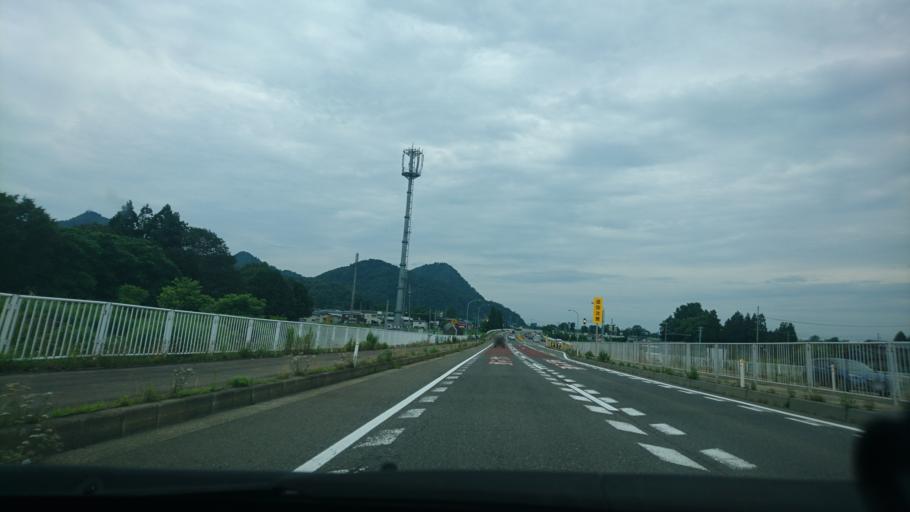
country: JP
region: Akita
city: Omagari
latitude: 39.4773
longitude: 140.4641
